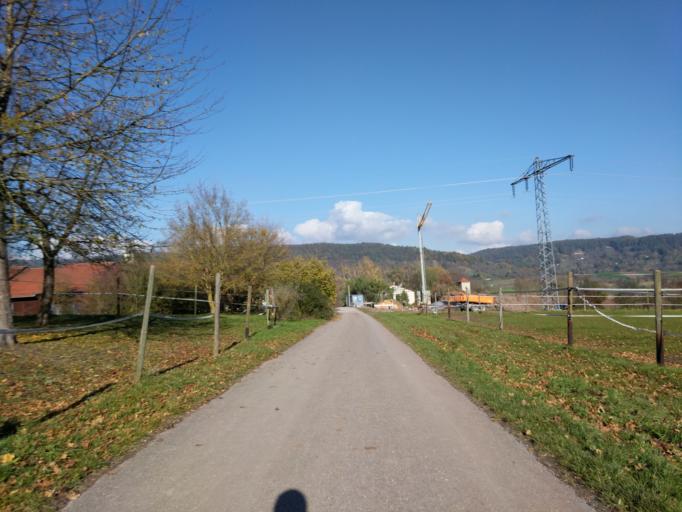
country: DE
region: Baden-Wuerttemberg
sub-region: Tuebingen Region
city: Tuebingen
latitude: 48.5162
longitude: 9.0010
